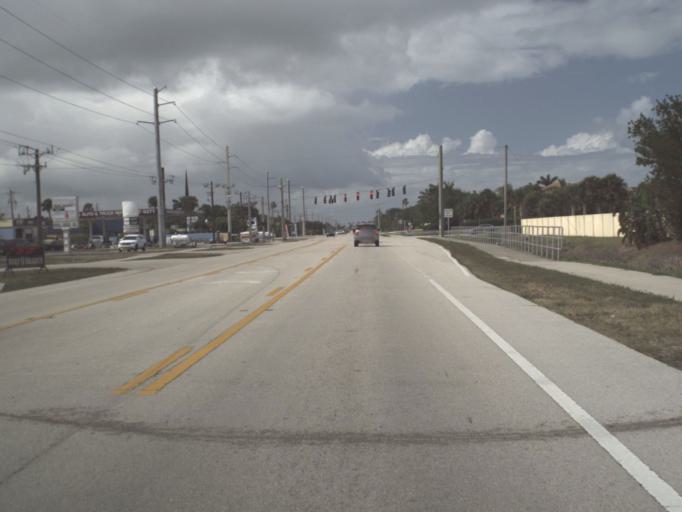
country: US
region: Florida
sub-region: Brevard County
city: South Patrick Shores
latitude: 28.1940
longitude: -80.6062
